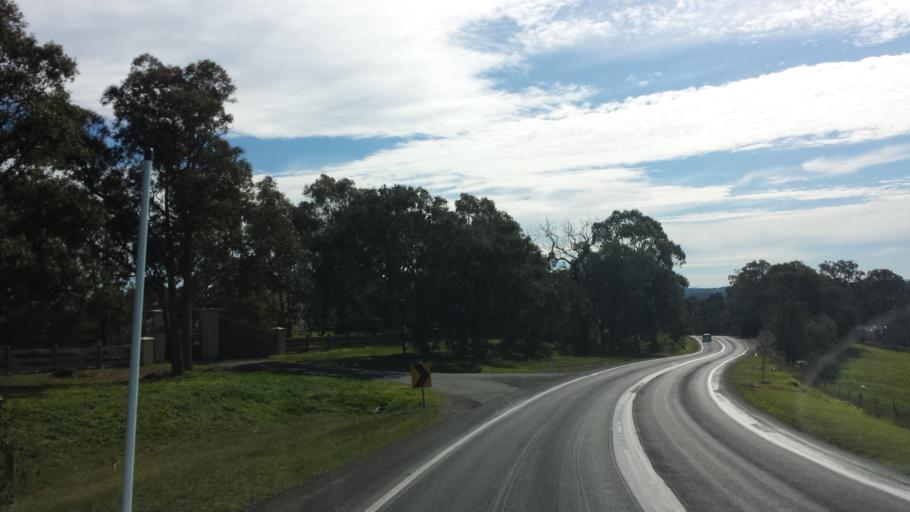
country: AU
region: Victoria
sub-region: Nillumbik
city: Research
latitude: -37.6852
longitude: 145.2104
